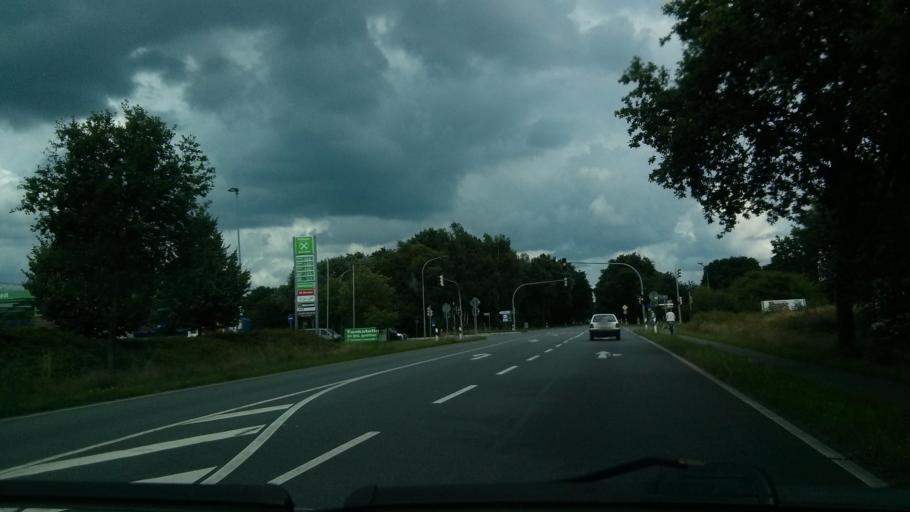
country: DE
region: Lower Saxony
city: Schiffdorf
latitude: 53.5260
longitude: 8.6457
